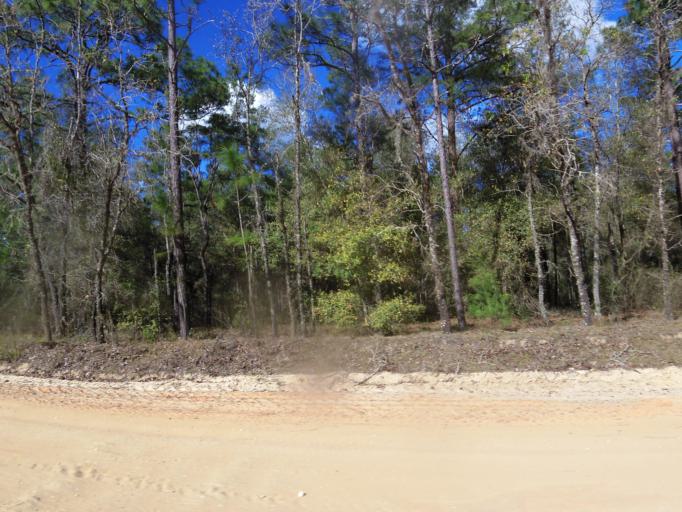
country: US
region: Florida
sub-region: Putnam County
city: Interlachen
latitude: 29.7840
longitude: -81.8646
